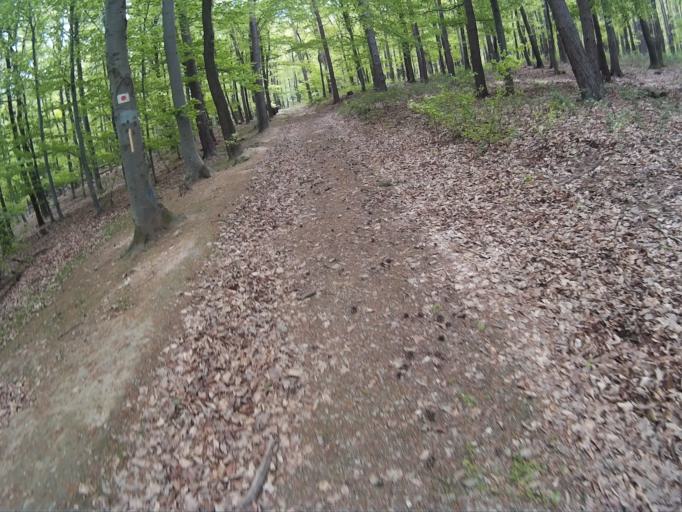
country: HU
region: Vas
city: Koszeg
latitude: 47.3621
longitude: 16.4972
